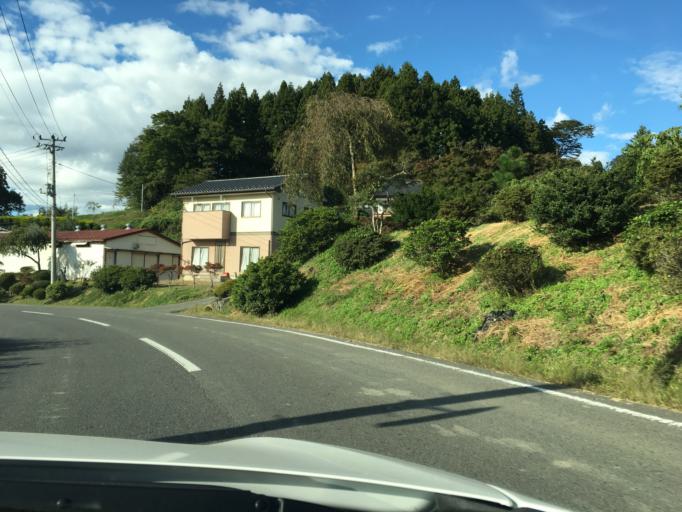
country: JP
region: Fukushima
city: Sukagawa
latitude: 37.2437
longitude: 140.4462
